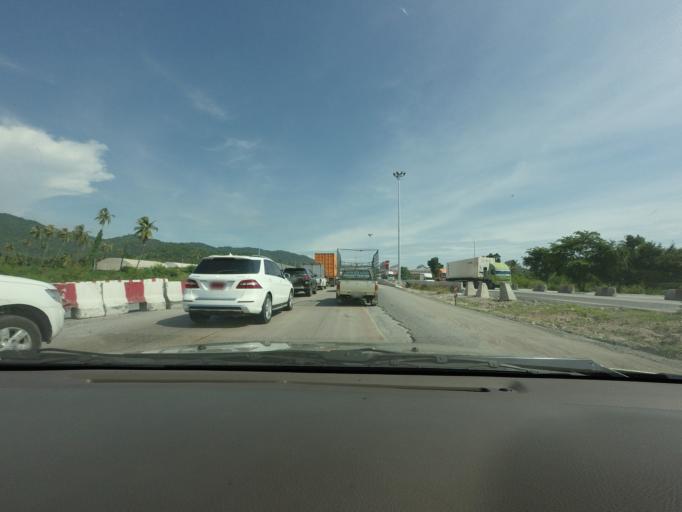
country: TH
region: Chon Buri
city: Chon Buri
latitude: 13.3108
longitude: 100.9929
